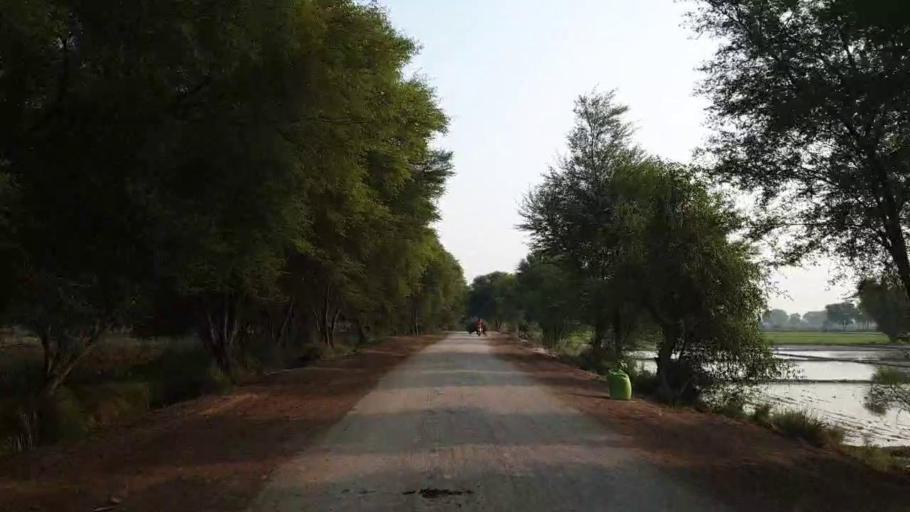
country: PK
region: Sindh
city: Bhan
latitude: 26.5024
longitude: 67.7603
